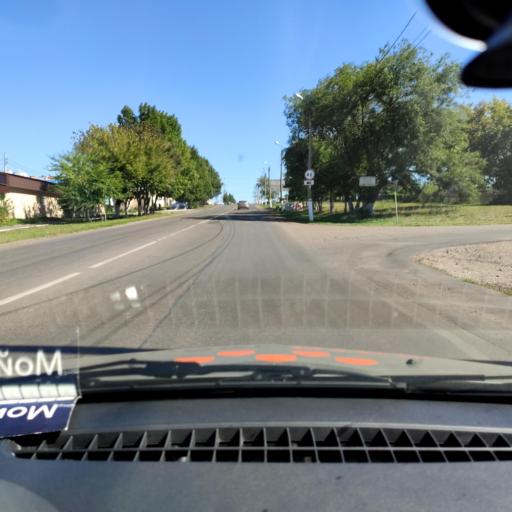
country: RU
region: Bashkortostan
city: Kumertau
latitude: 52.7569
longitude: 55.8135
